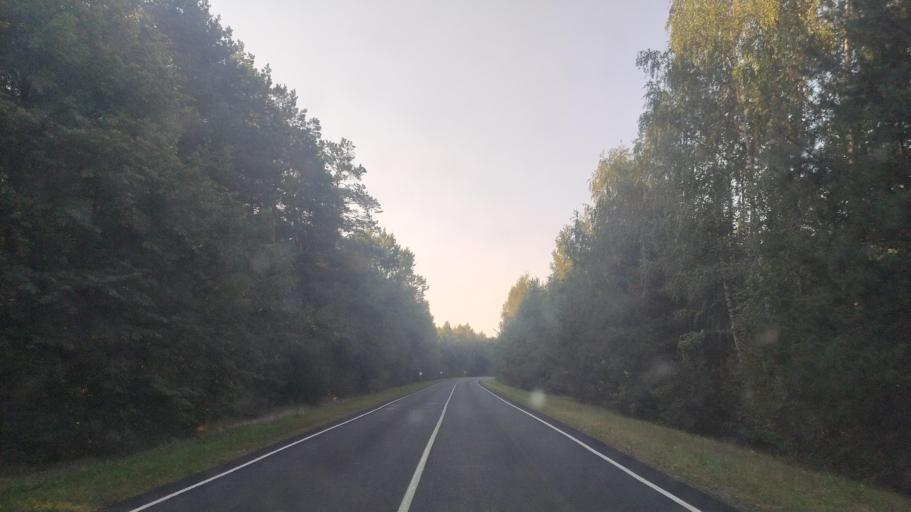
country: BY
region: Brest
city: Drahichyn
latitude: 52.2791
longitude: 25.0713
